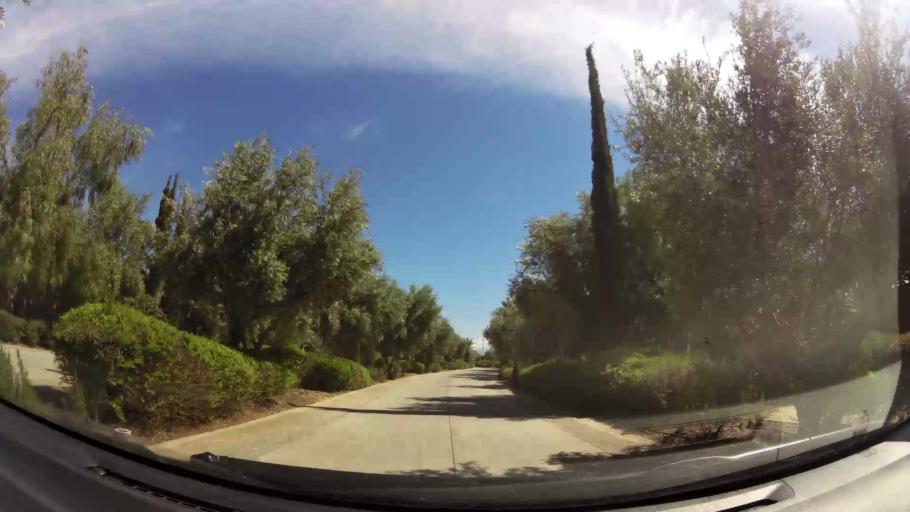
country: MA
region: Marrakech-Tensift-Al Haouz
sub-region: Marrakech
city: Marrakesh
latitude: 31.6032
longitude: -7.9533
